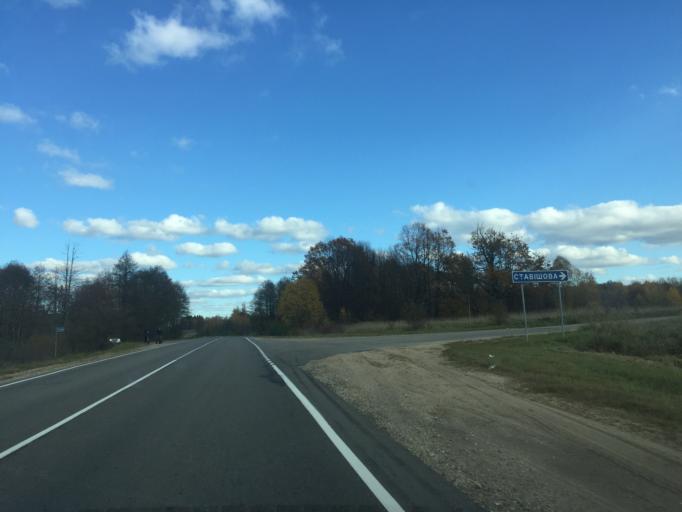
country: BY
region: Minsk
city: Narach
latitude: 54.9954
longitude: 26.7848
